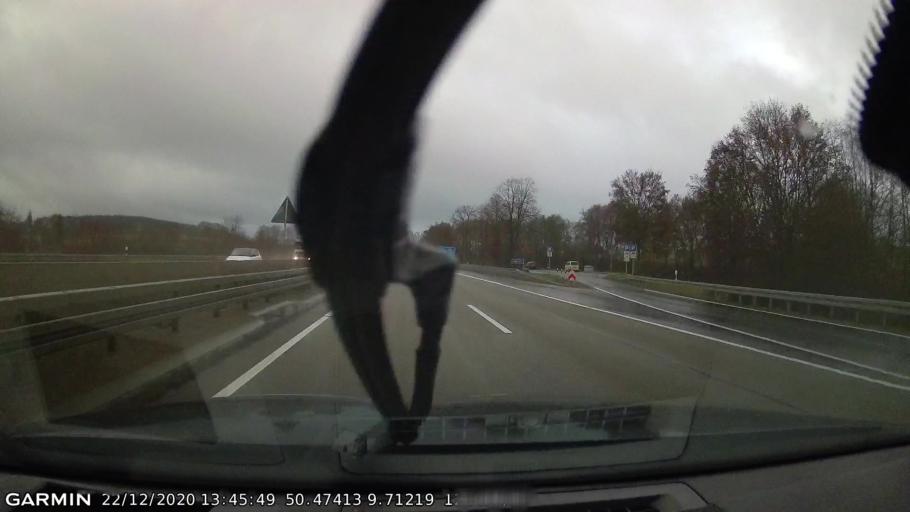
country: DE
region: Hesse
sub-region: Regierungsbezirk Kassel
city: Eichenzell
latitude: 50.4738
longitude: 9.7123
